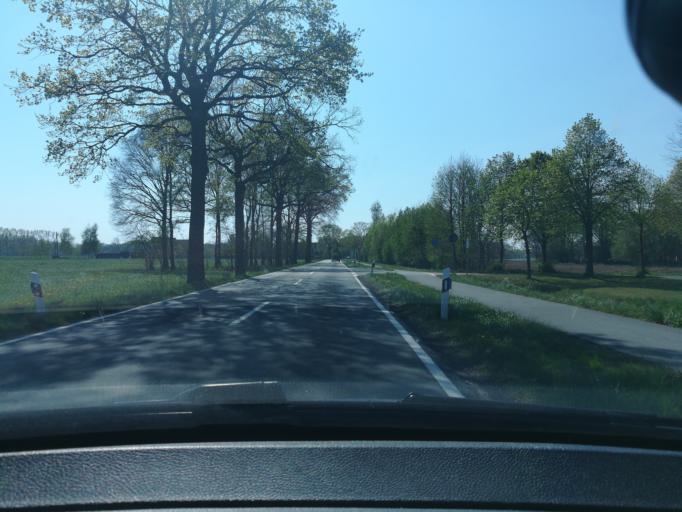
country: DE
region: North Rhine-Westphalia
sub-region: Regierungsbezirk Detmold
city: Harsewinkel
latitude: 52.0309
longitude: 8.2616
